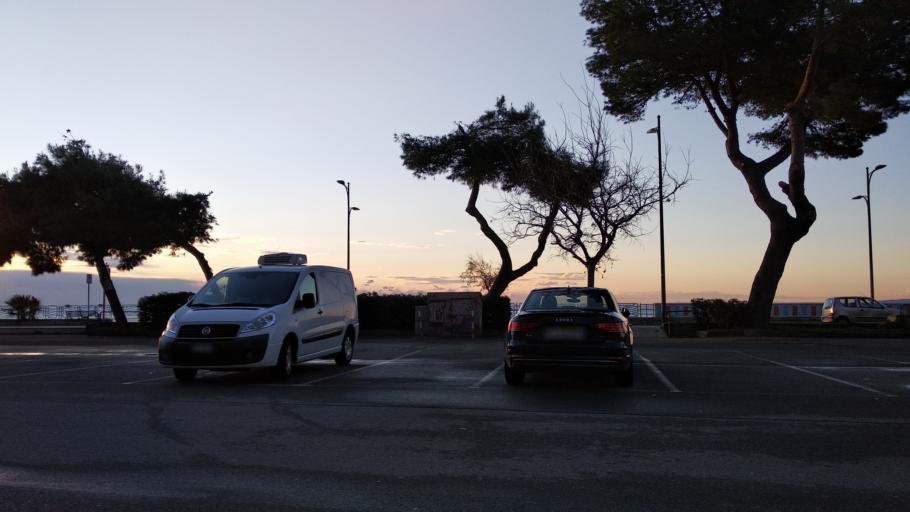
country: IT
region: Calabria
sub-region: Provincia di Catanzaro
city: Barone
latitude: 38.8270
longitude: 16.6268
